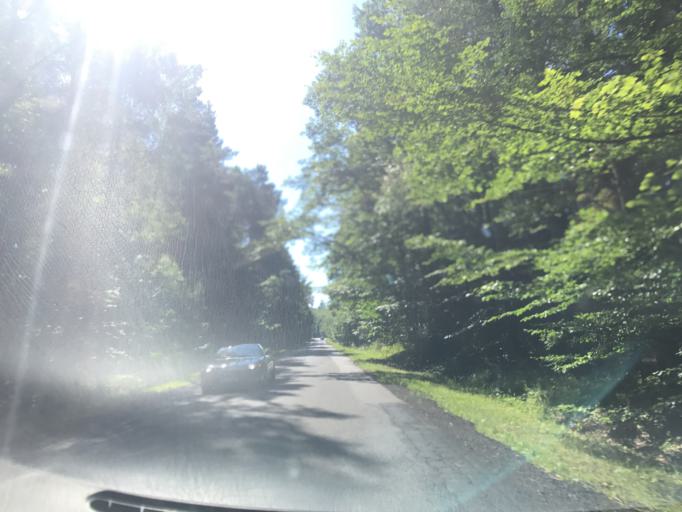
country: PL
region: Pomeranian Voivodeship
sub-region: Powiat bytowski
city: Czarna Dabrowka
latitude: 54.3788
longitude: 17.4916
